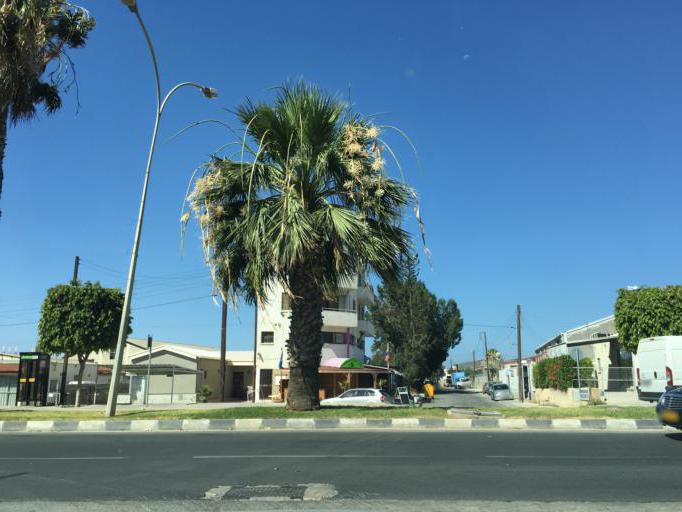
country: CY
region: Limassol
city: Limassol
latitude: 34.6621
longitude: 33.0180
